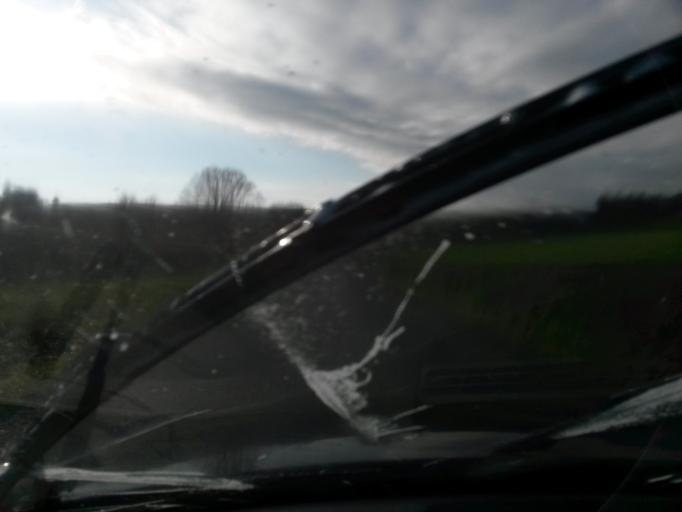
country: DE
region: Bavaria
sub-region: Regierungsbezirk Unterfranken
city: Rimpar
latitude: 49.8483
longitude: 9.9461
